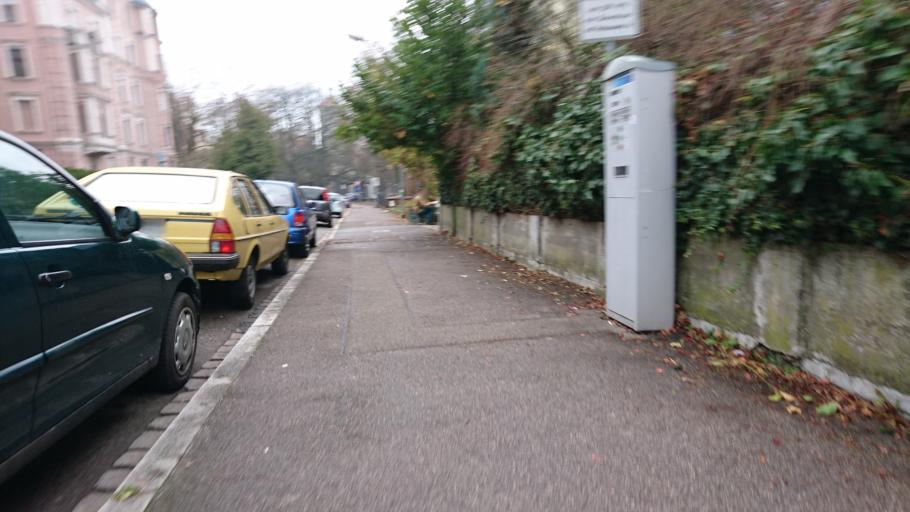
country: DE
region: Bavaria
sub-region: Swabia
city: Augsburg
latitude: 48.3779
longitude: 10.8905
